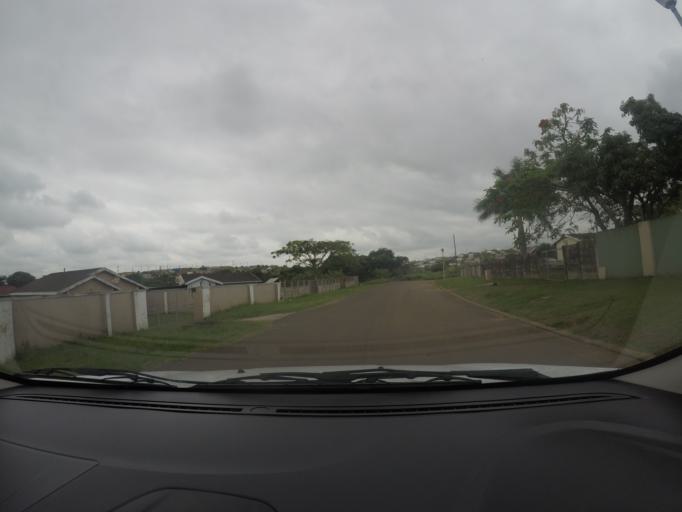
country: ZA
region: KwaZulu-Natal
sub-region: uThungulu District Municipality
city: Empangeni
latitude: -28.7623
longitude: 31.8827
